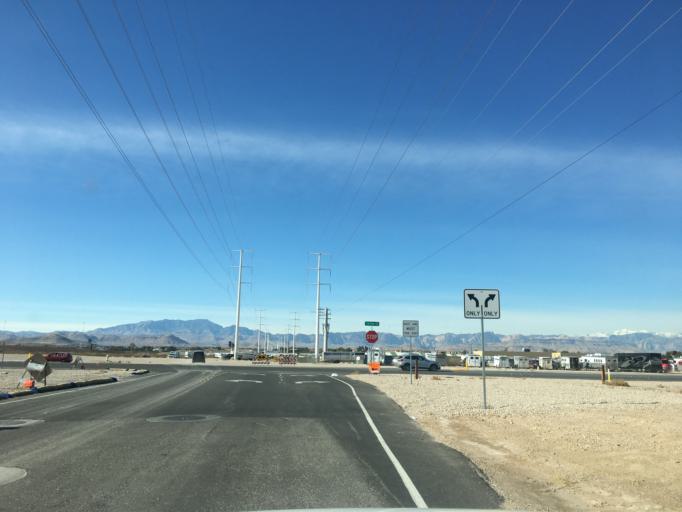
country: US
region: Nevada
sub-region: Clark County
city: Enterprise
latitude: 36.0028
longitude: -115.1718
